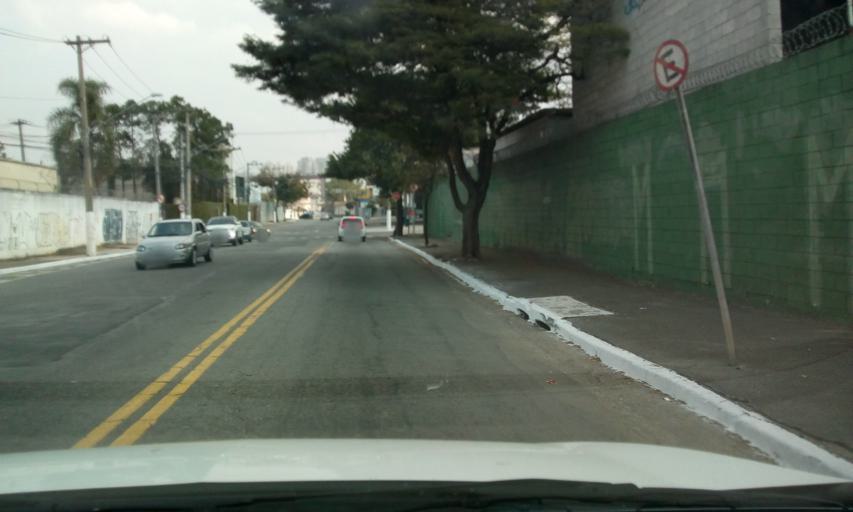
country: BR
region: Sao Paulo
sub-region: Osasco
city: Osasco
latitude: -23.5449
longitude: -46.7379
